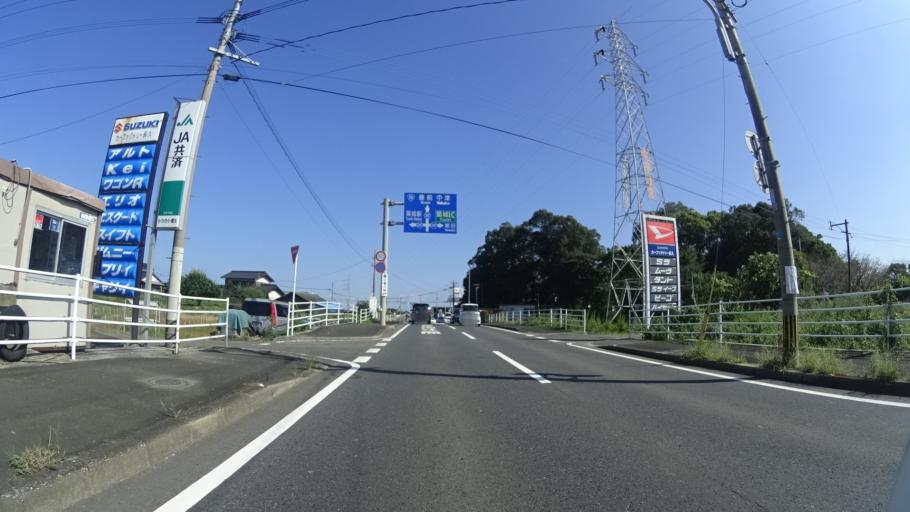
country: JP
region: Fukuoka
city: Tsuiki
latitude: 33.6692
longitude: 131.0214
